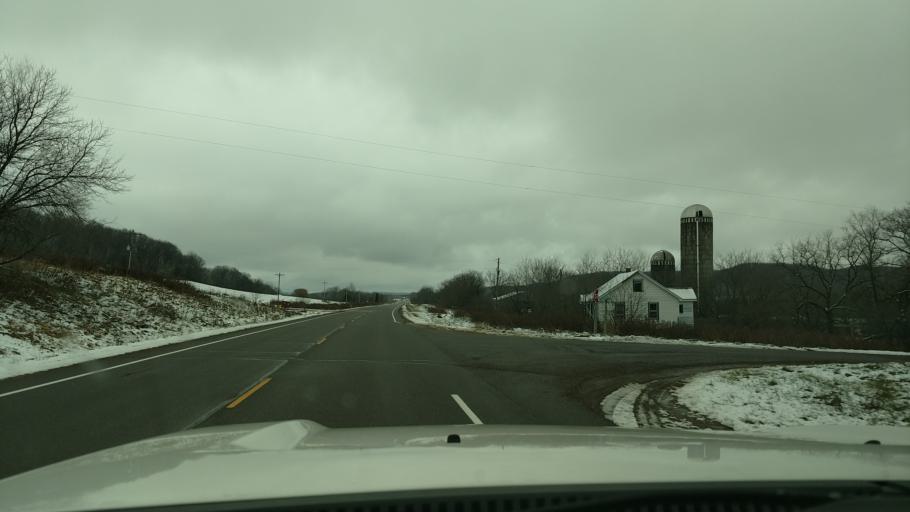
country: US
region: Wisconsin
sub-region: Dunn County
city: Colfax
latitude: 45.1369
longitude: -91.7971
